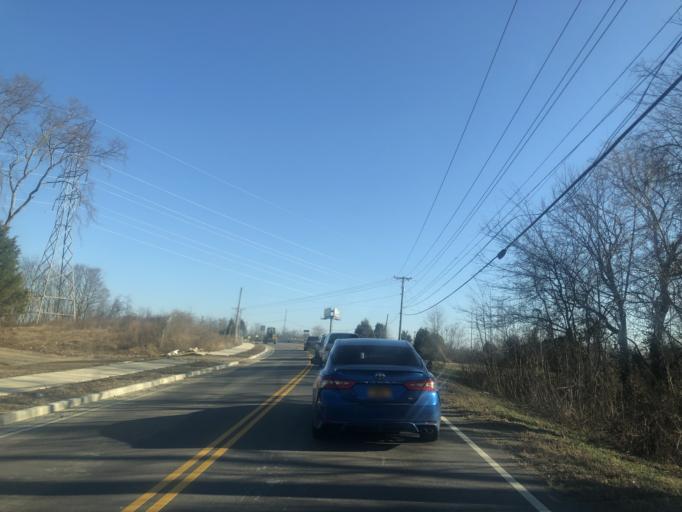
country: US
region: Tennessee
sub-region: Rutherford County
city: La Vergne
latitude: 36.0303
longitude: -86.6411
